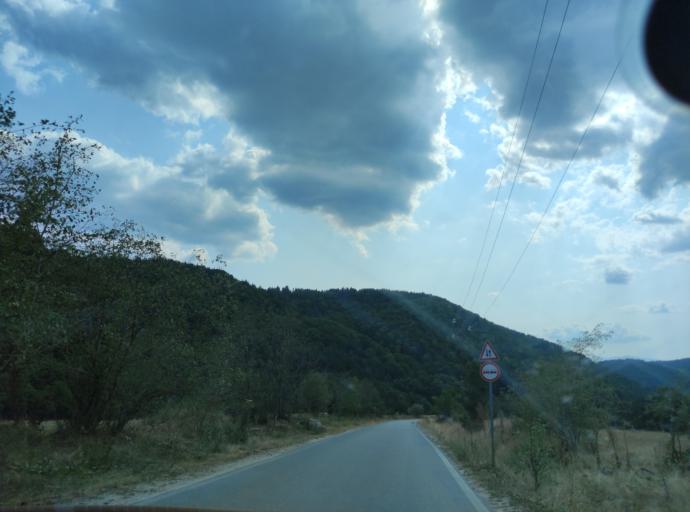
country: BG
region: Blagoevgrad
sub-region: Obshtina Belitsa
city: Belitsa
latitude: 42.0111
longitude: 23.5667
